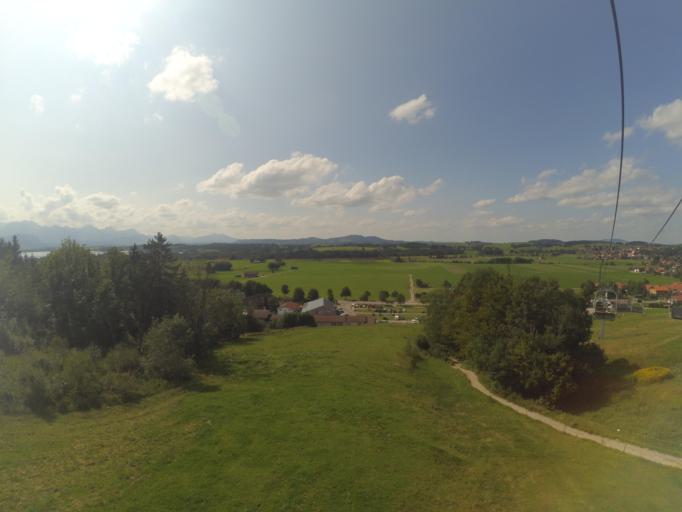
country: DE
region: Bavaria
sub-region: Swabia
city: Halblech
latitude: 47.6126
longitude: 10.8071
